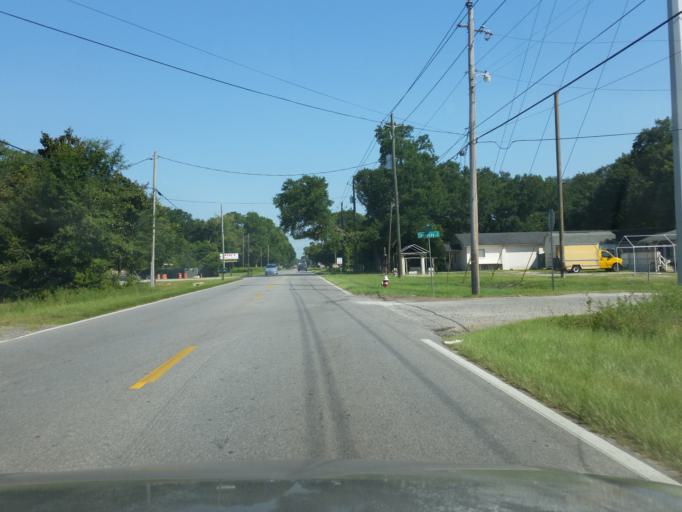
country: US
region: Florida
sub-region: Escambia County
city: Ensley
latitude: 30.5375
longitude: -87.2760
